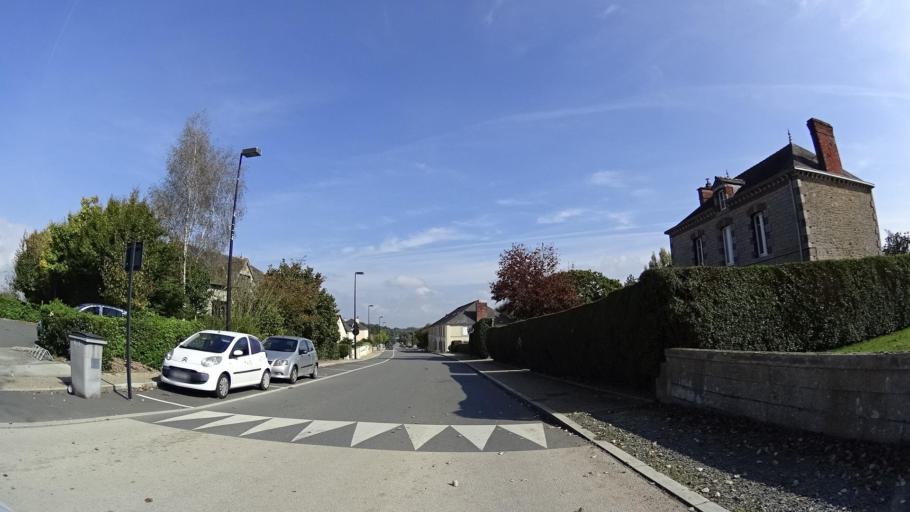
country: FR
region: Brittany
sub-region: Departement d'Ille-et-Vilaine
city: Medreac
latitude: 48.2678
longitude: -2.0618
